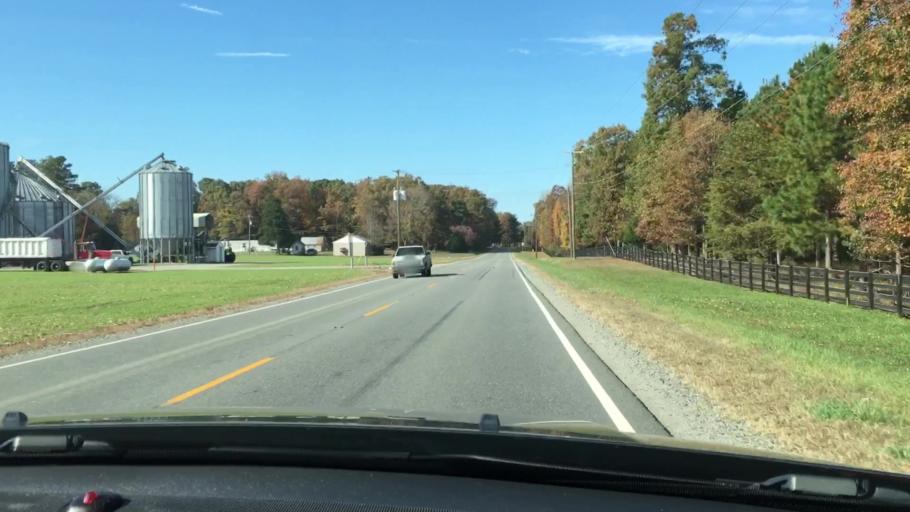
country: US
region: Virginia
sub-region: King and Queen County
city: King and Queen Court House
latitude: 37.5948
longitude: -76.9016
